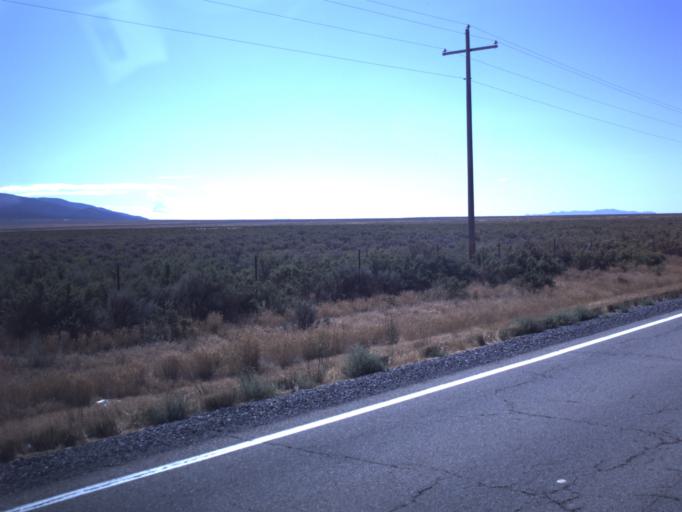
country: US
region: Utah
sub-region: Tooele County
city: Tooele
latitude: 40.3965
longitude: -112.3861
